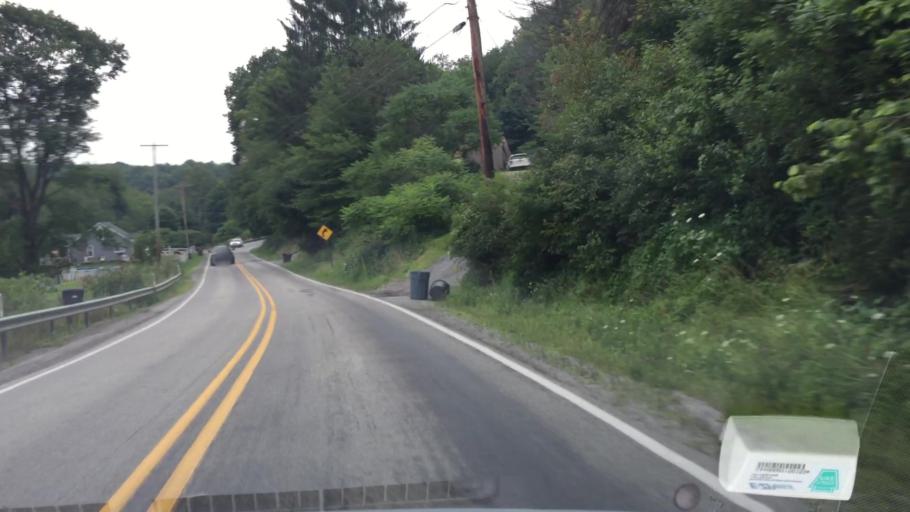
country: US
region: Pennsylvania
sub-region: Allegheny County
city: Curtisville
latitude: 40.6897
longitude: -79.8368
